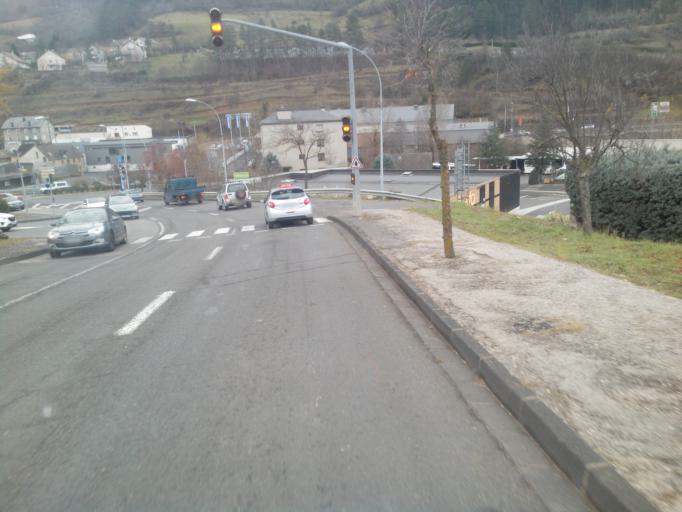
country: FR
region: Languedoc-Roussillon
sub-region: Departement de la Lozere
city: Mende
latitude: 44.5182
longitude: 3.4870
